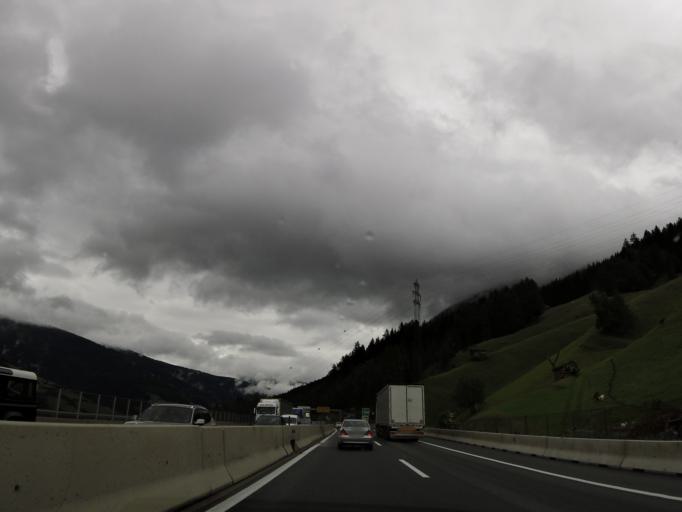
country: AT
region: Tyrol
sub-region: Politischer Bezirk Innsbruck Land
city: Schoenberg im Stubaital
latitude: 47.1822
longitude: 11.4102
